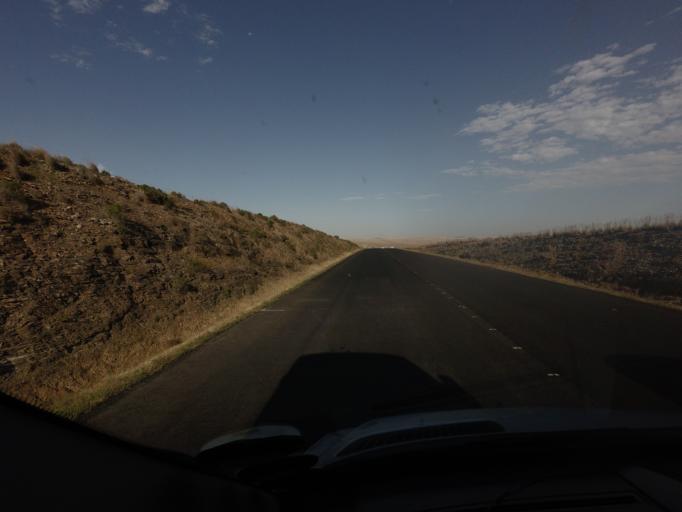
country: ZA
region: Western Cape
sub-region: Overberg District Municipality
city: Swellendam
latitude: -34.1068
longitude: 20.3449
